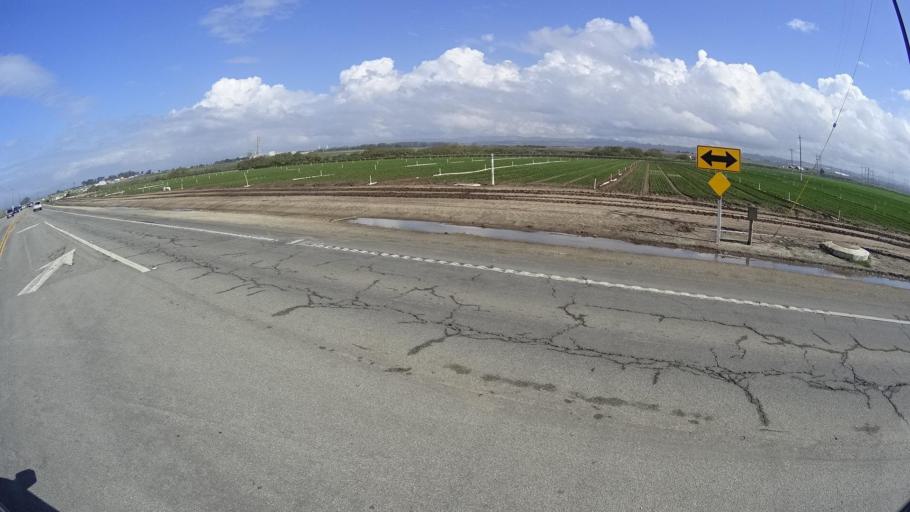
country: US
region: California
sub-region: Monterey County
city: Castroville
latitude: 36.7787
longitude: -121.7780
